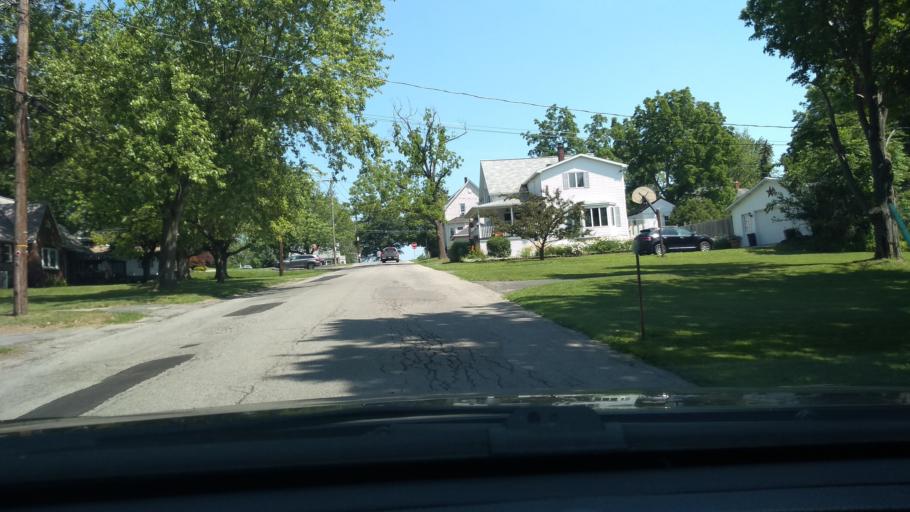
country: US
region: New York
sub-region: Erie County
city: West Seneca
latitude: 42.8316
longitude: -78.7592
